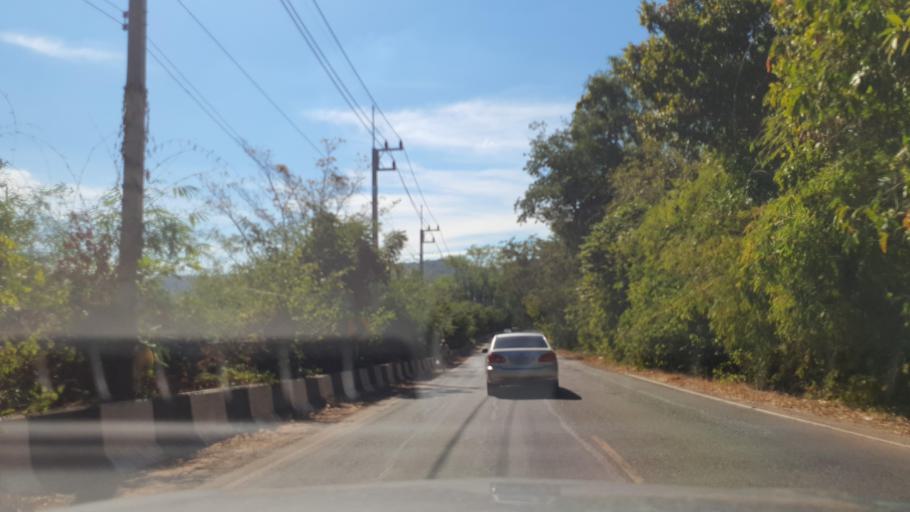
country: TH
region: Kalasin
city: Khao Wong
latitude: 16.7629
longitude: 104.1546
